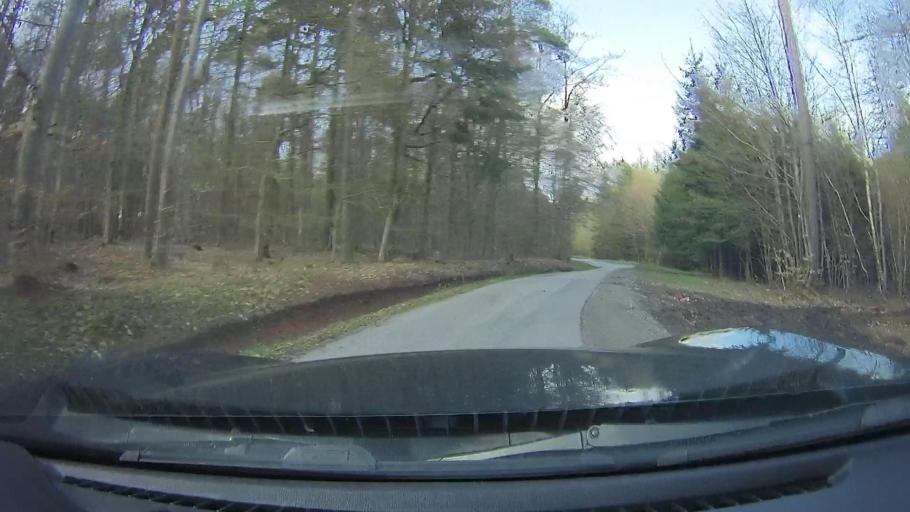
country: DE
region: Bavaria
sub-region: Regierungsbezirk Unterfranken
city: Weilbach
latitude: 49.6089
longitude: 9.2784
